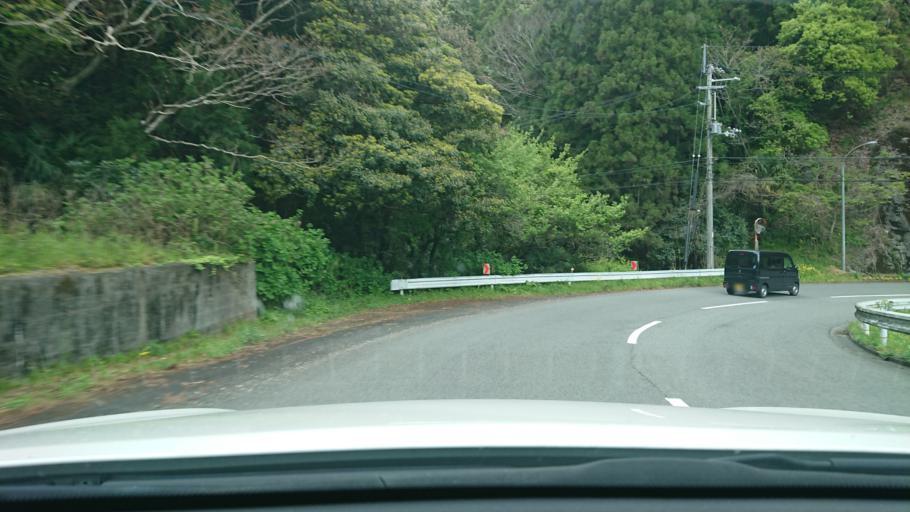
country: JP
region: Tokushima
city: Ishii
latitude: 33.9166
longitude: 134.4245
